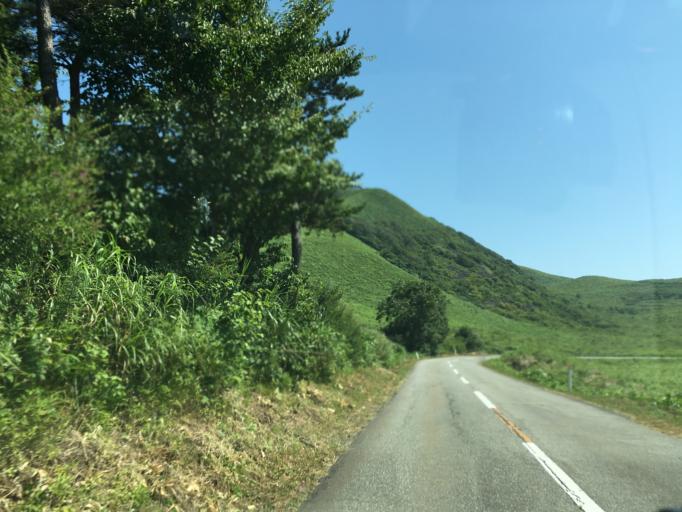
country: JP
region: Akita
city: Tenno
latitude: 39.9393
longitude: 139.8707
